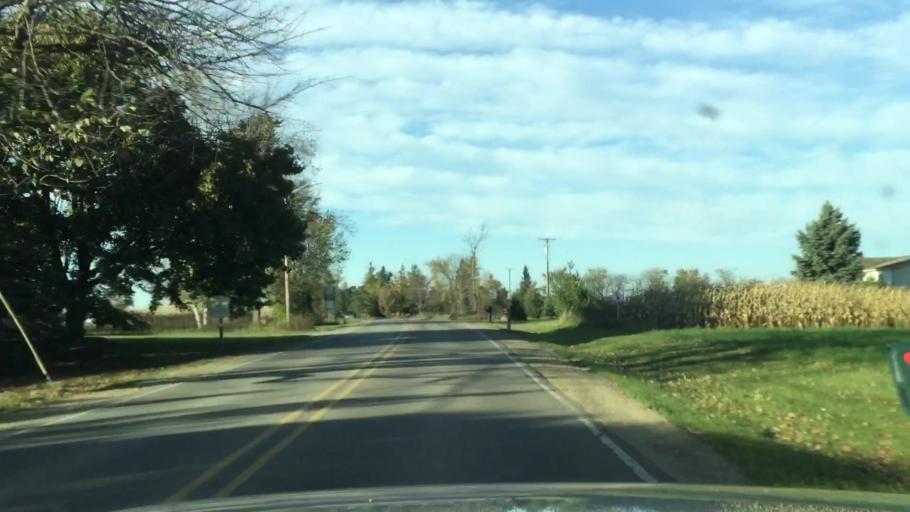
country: US
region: Michigan
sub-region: Lapeer County
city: North Branch
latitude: 43.2359
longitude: -83.1959
